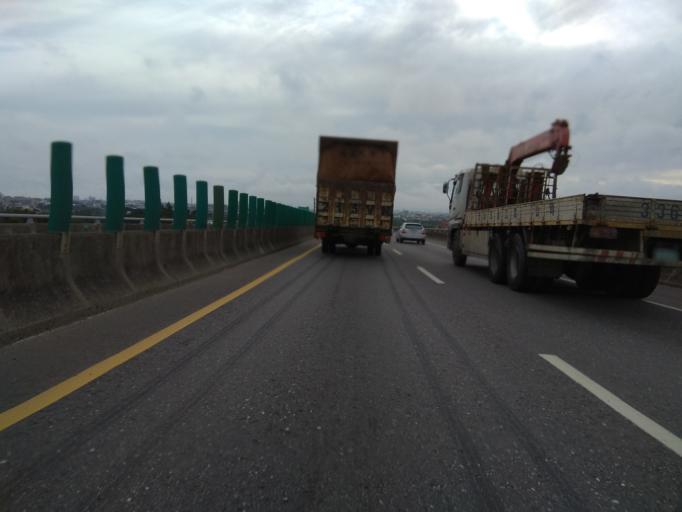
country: TW
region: Taiwan
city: Daxi
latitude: 24.9299
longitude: 121.2026
